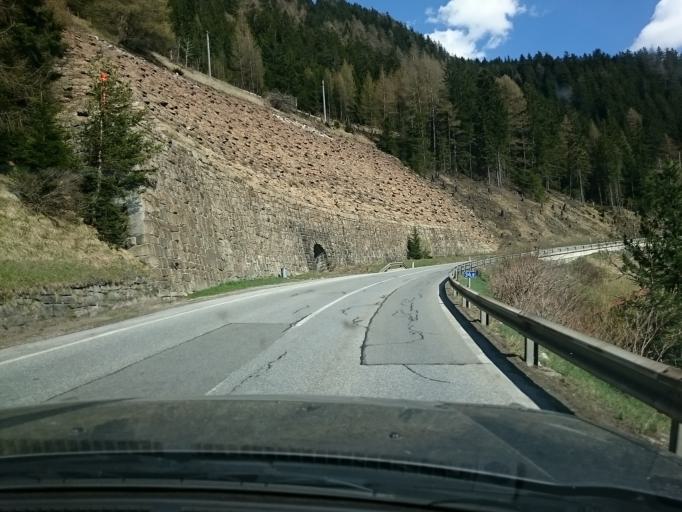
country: AT
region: Tyrol
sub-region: Politischer Bezirk Innsbruck Land
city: Gries am Brenner
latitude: 47.0271
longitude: 11.5006
